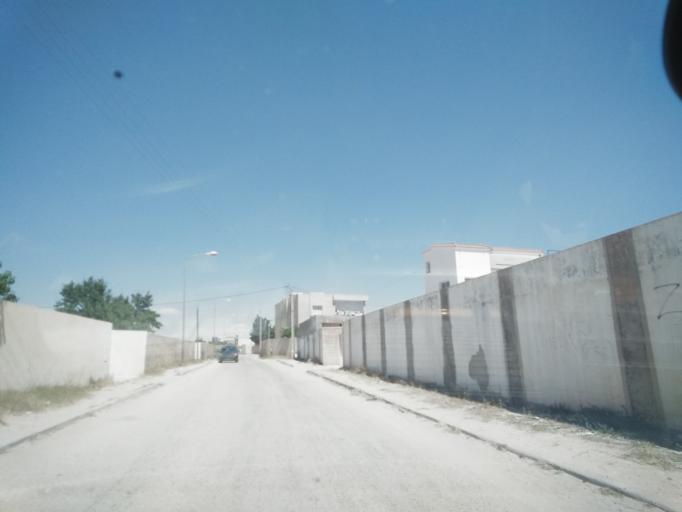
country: TN
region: Safaqis
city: Al Qarmadah
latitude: 34.8210
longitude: 10.7673
